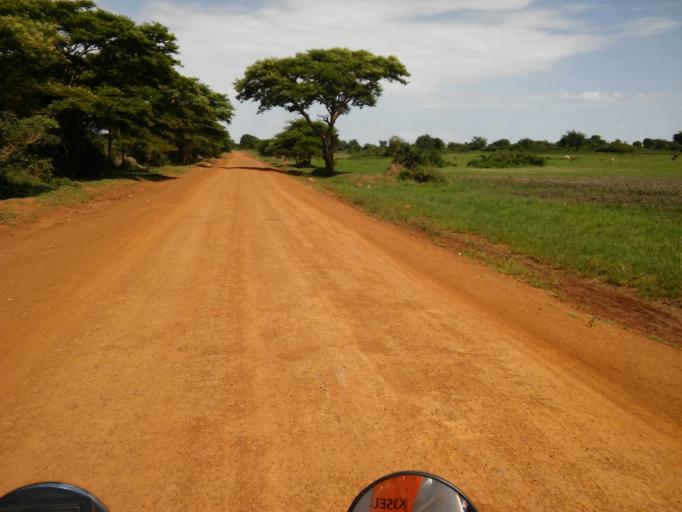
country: UG
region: Eastern Region
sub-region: Kumi District
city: Kumi
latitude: 1.4841
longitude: 33.9123
